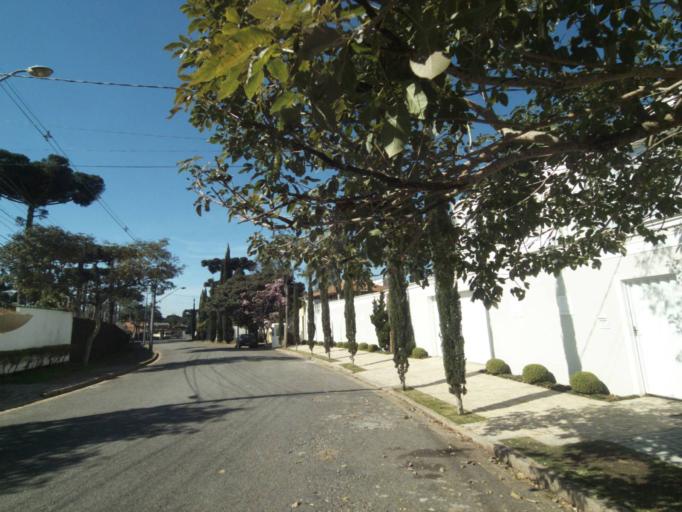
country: BR
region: Parana
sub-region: Curitiba
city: Curitiba
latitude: -25.4171
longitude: -49.2322
